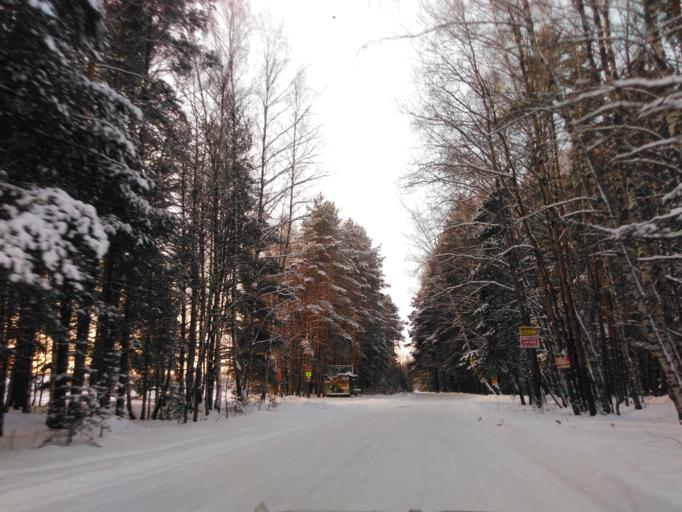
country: RU
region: Tverskaya
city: Konakovo
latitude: 56.6554
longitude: 36.6590
